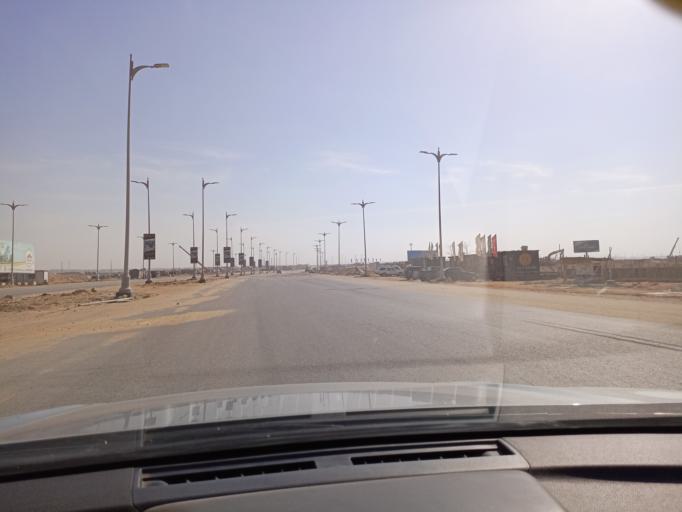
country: EG
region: Muhafazat al Qalyubiyah
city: Al Khankah
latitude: 30.0278
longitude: 31.6791
